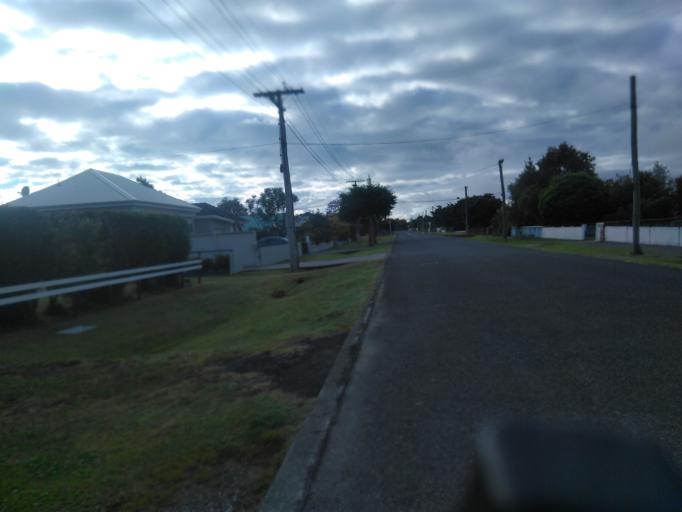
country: NZ
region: Gisborne
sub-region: Gisborne District
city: Gisborne
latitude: -38.6549
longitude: 178.0270
